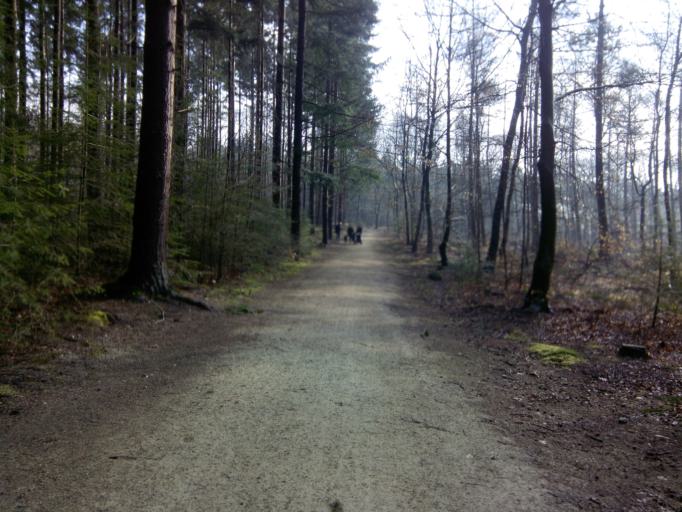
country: NL
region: Utrecht
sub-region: Gemeente Utrechtse Heuvelrug
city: Amerongen
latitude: 52.0109
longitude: 5.4523
